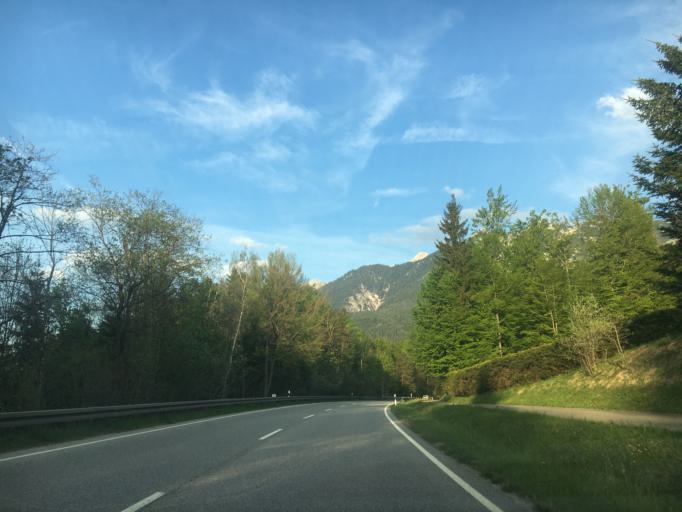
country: DE
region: Bavaria
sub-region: Upper Bavaria
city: Krun
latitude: 47.5002
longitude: 11.2675
